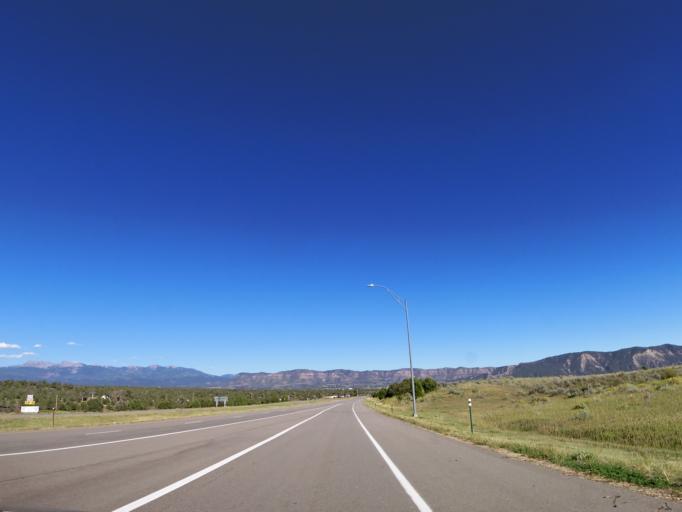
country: US
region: Colorado
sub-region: Montezuma County
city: Mancos
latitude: 37.3394
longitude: -108.4085
